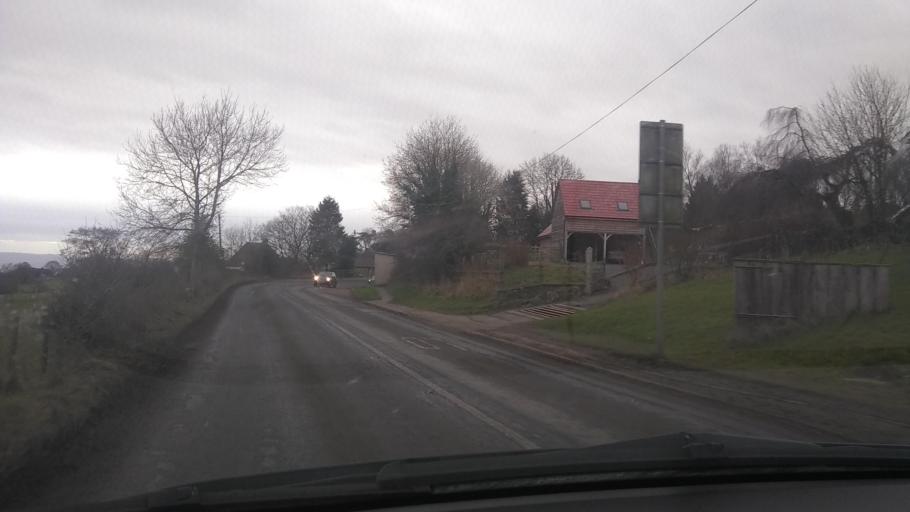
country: GB
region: England
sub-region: Shropshire
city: Cleobury Mortimer
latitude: 52.3866
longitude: -2.5591
